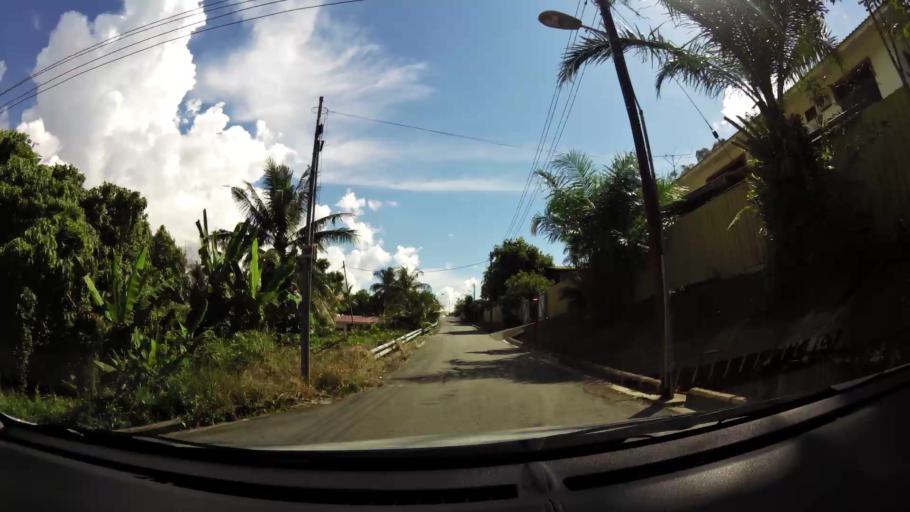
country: BN
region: Brunei and Muara
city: Bandar Seri Begawan
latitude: 4.9581
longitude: 114.9472
